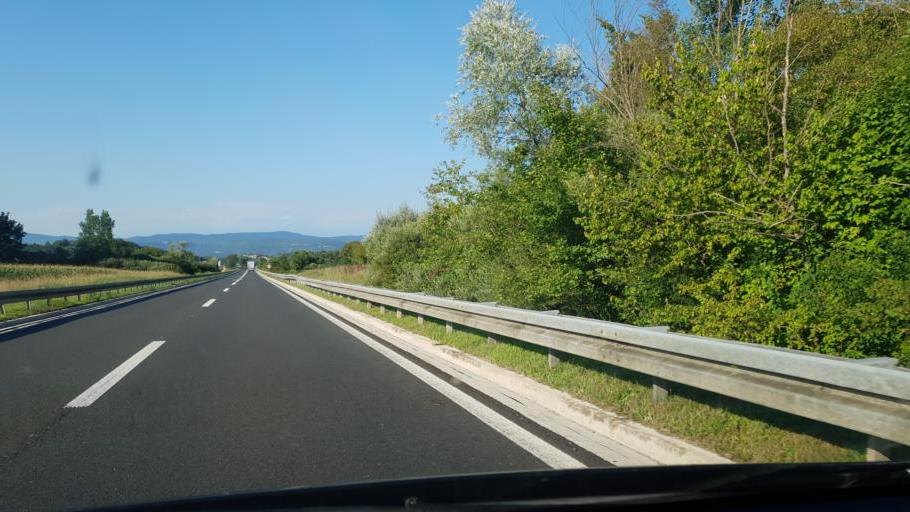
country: HR
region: Istarska
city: Pazin
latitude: 45.2971
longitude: 14.0460
